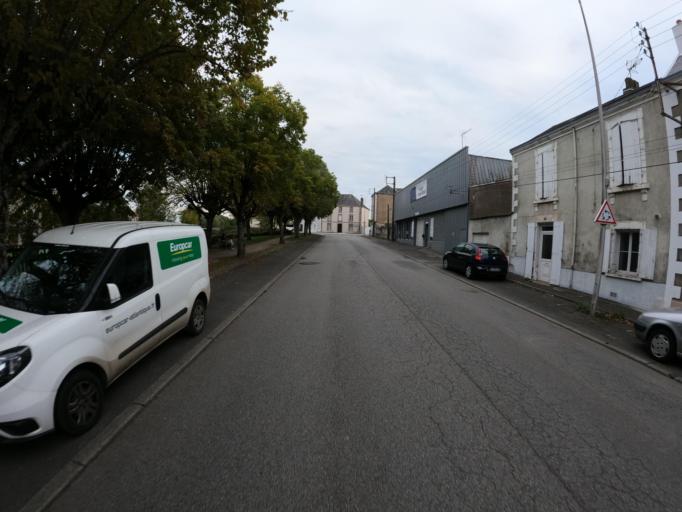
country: FR
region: Poitou-Charentes
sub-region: Departement des Deux-Sevres
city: Parthenay
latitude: 46.6466
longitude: -0.2398
